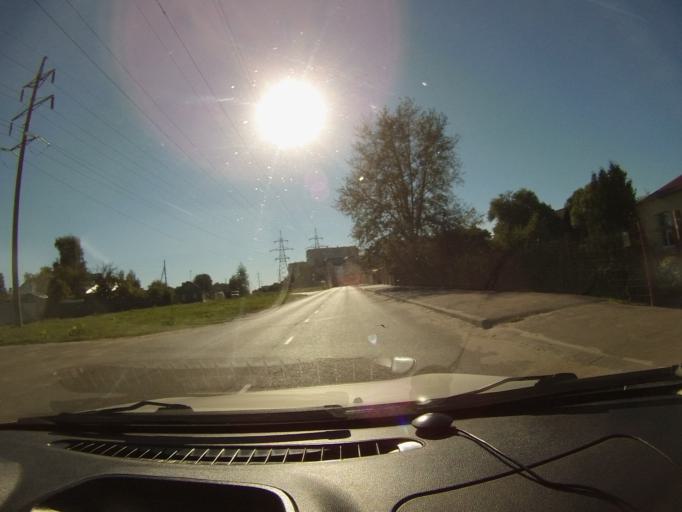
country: RU
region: Tambov
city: Tambov
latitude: 52.7598
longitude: 41.4194
